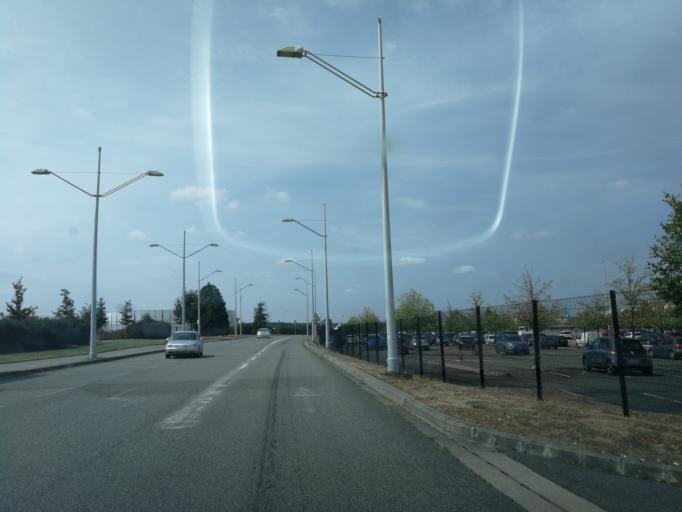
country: FR
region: Midi-Pyrenees
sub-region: Departement de la Haute-Garonne
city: Beauzelle
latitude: 43.6453
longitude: 1.3636
